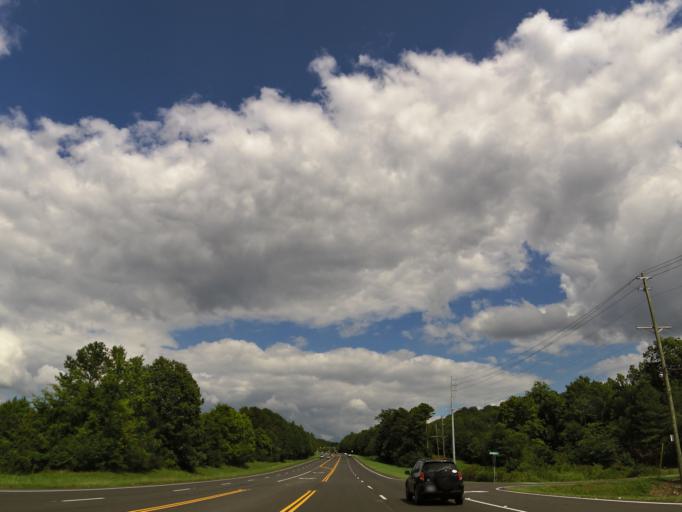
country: US
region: Georgia
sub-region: Walker County
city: Fairview
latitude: 34.9508
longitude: -85.3077
